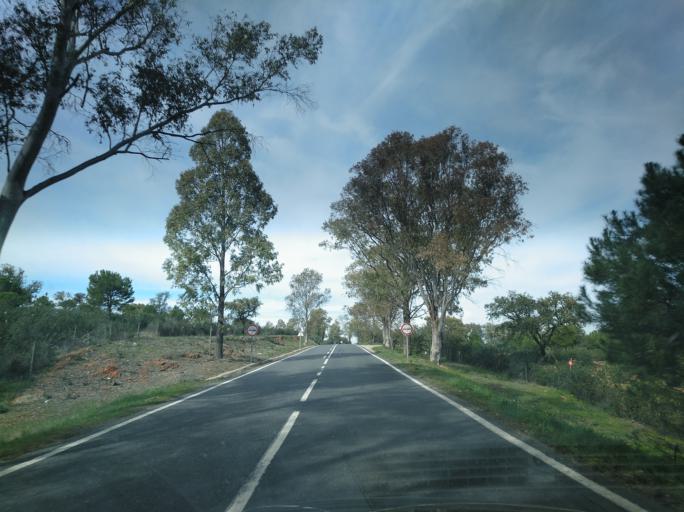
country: PT
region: Beja
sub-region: Mertola
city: Mertola
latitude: 37.7152
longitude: -7.7555
